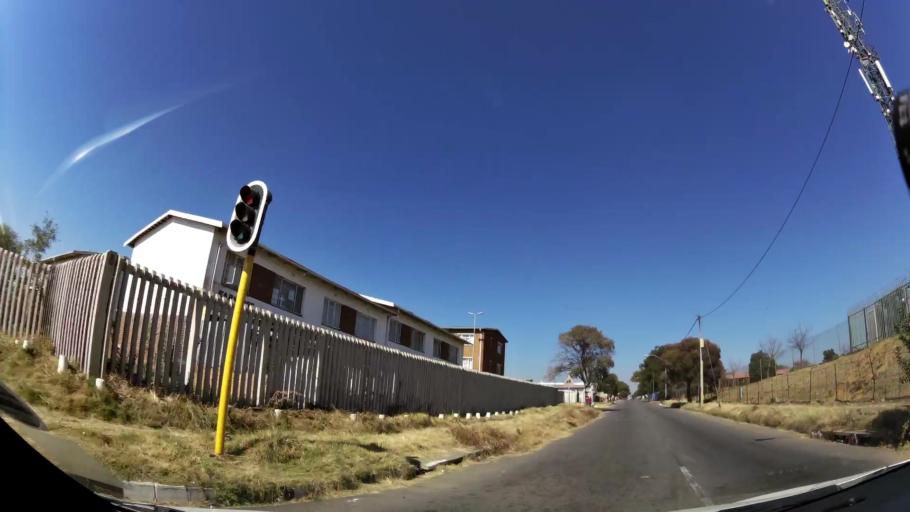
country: ZA
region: Gauteng
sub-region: City of Johannesburg Metropolitan Municipality
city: Johannesburg
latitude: -26.2437
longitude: 28.0927
